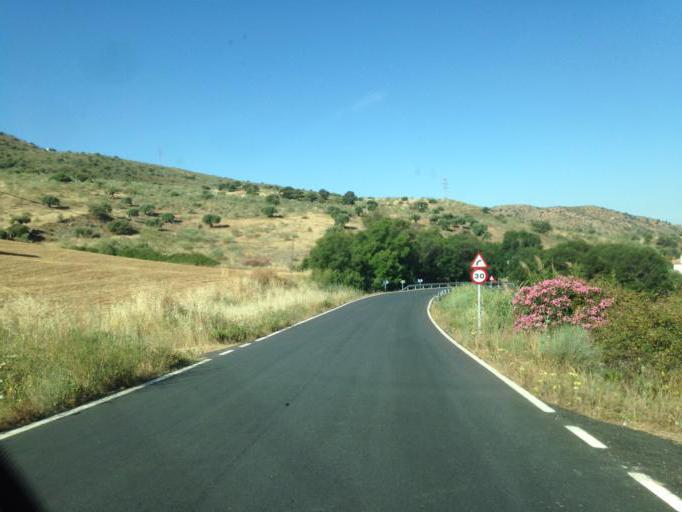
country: ES
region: Andalusia
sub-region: Provincia de Malaga
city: Casabermeja
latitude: 36.9015
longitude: -4.4492
